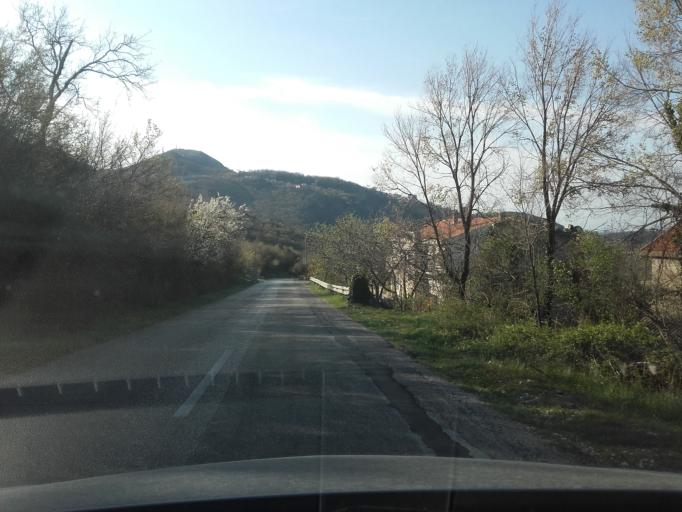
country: ME
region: Budva
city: Budva
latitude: 42.3047
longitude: 18.8091
